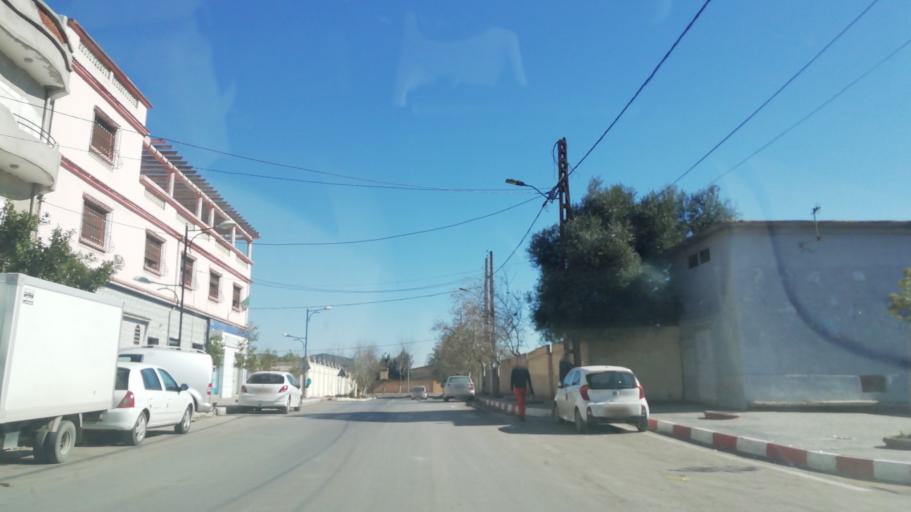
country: DZ
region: Oran
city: Es Senia
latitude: 35.6542
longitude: -0.6168
